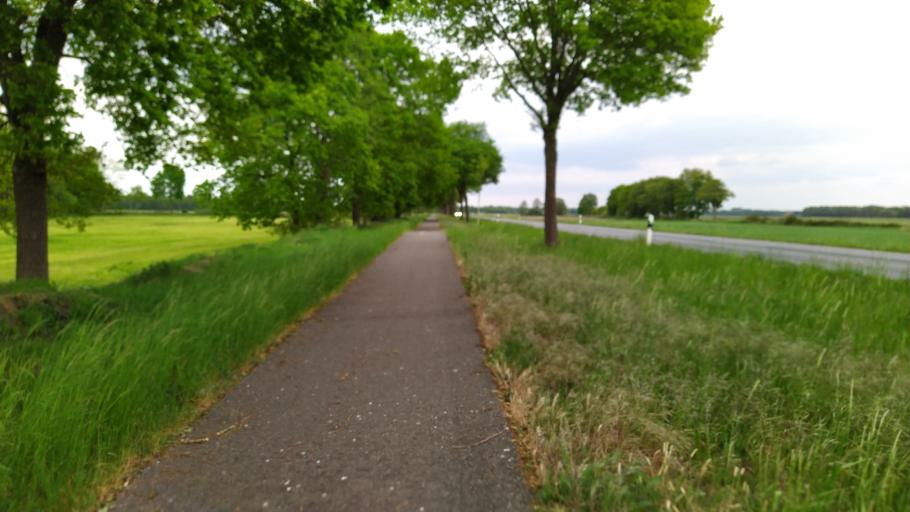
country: DE
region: Lower Saxony
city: Tarmstedt
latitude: 53.2041
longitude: 9.0333
